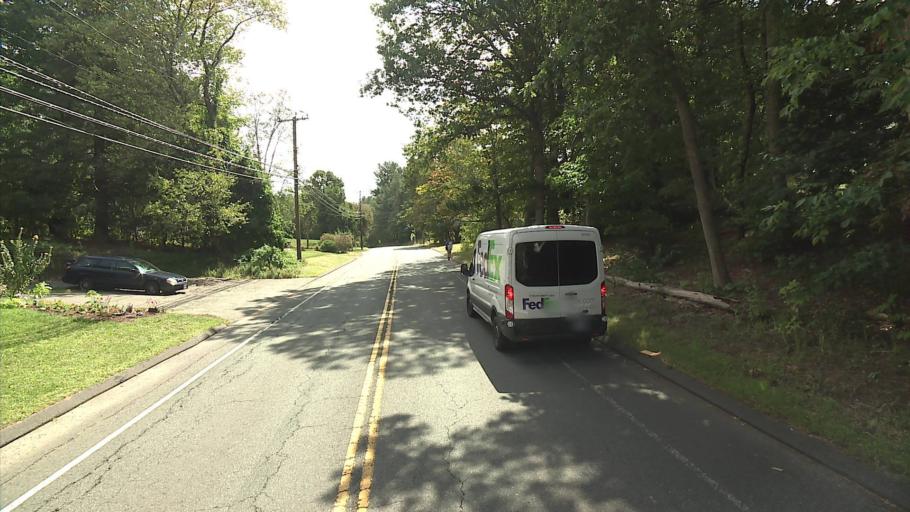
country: US
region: Connecticut
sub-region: Hartford County
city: Salmon Brook
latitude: 41.9613
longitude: -72.7996
